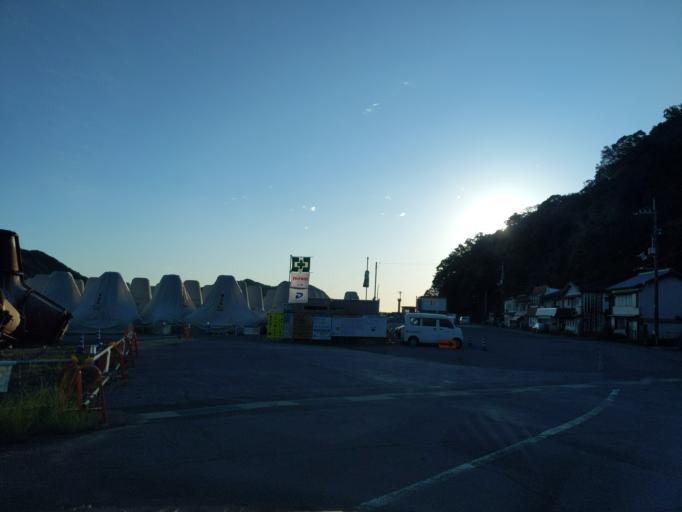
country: JP
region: Kochi
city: Muroto-misakicho
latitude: 33.5434
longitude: 134.2995
